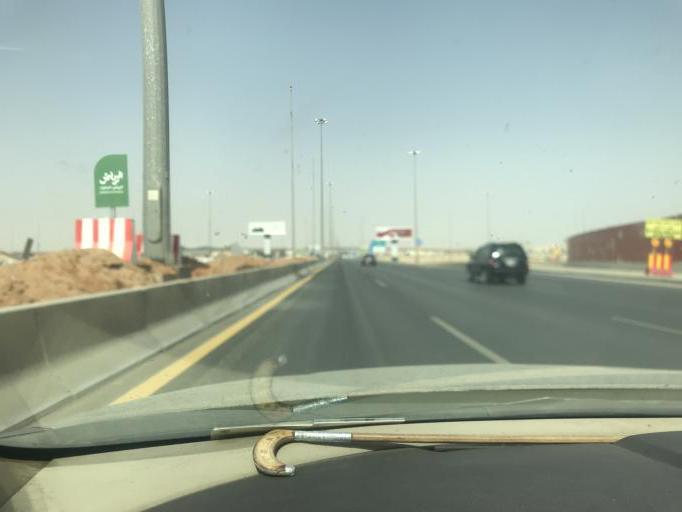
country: SA
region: Ar Riyad
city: Riyadh
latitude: 24.8241
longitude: 46.6078
